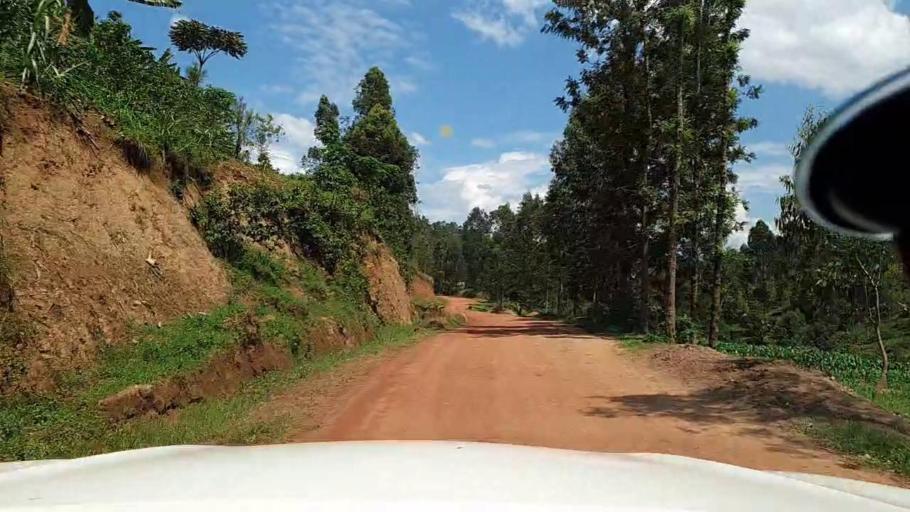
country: RW
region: Kigali
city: Kigali
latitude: -1.7725
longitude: 29.8742
